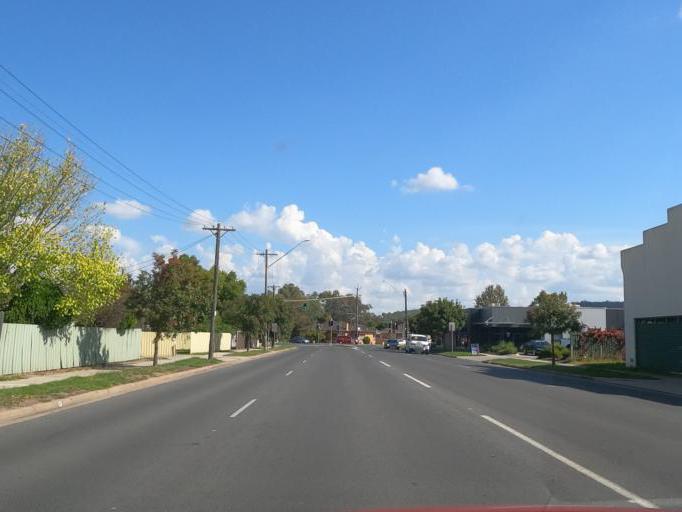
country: AU
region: New South Wales
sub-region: Albury Municipality
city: North Albury
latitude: -36.0563
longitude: 146.9281
